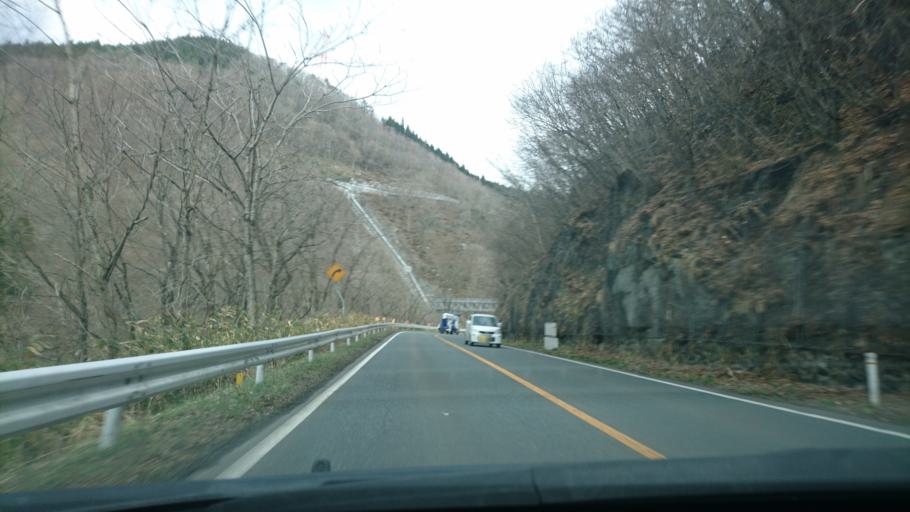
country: JP
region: Iwate
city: Hanamaki
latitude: 39.3620
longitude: 141.2960
